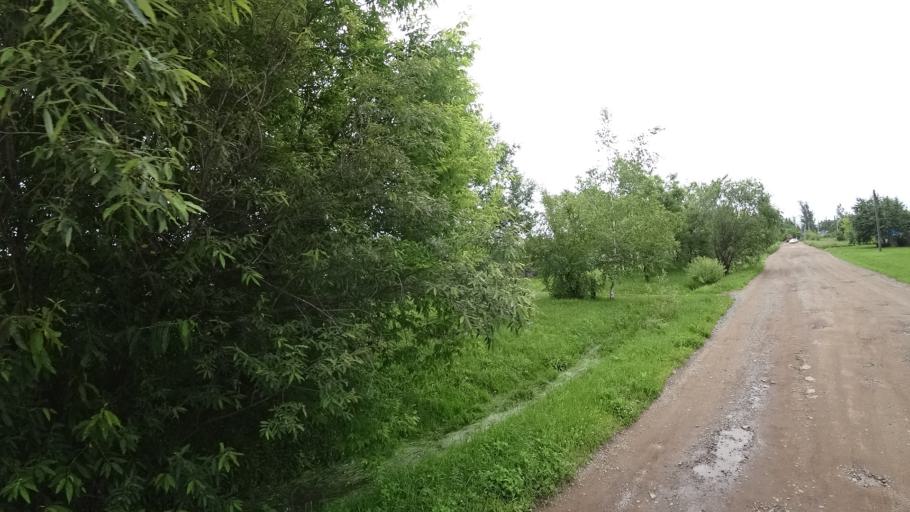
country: RU
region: Primorskiy
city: Novosysoyevka
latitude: 44.2497
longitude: 133.3768
